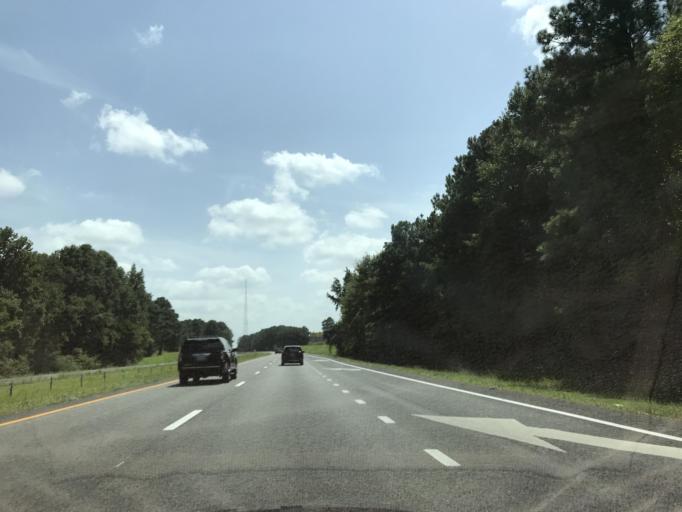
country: US
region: North Carolina
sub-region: Sampson County
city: Plain View
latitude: 35.2453
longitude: -78.3743
